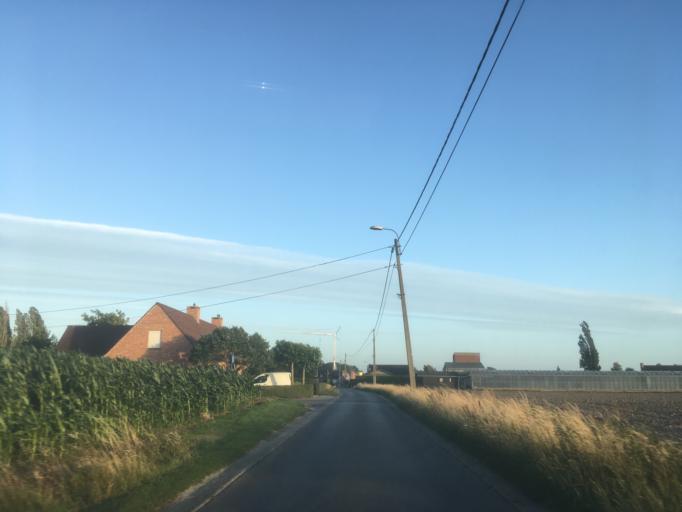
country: BE
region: Flanders
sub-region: Provincie West-Vlaanderen
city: Hooglede
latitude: 51.0178
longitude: 3.0950
